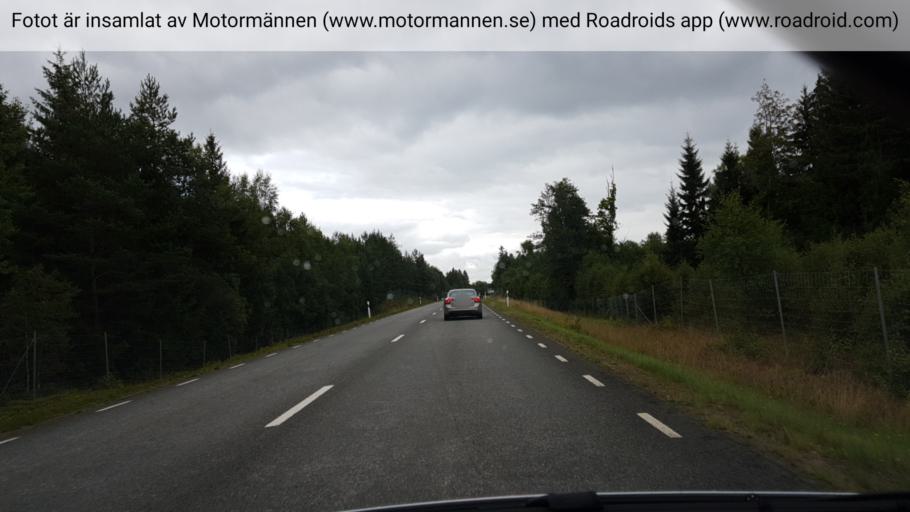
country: SE
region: Vaestra Goetaland
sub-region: Skara Kommun
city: Skara
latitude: 58.3438
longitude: 13.4340
